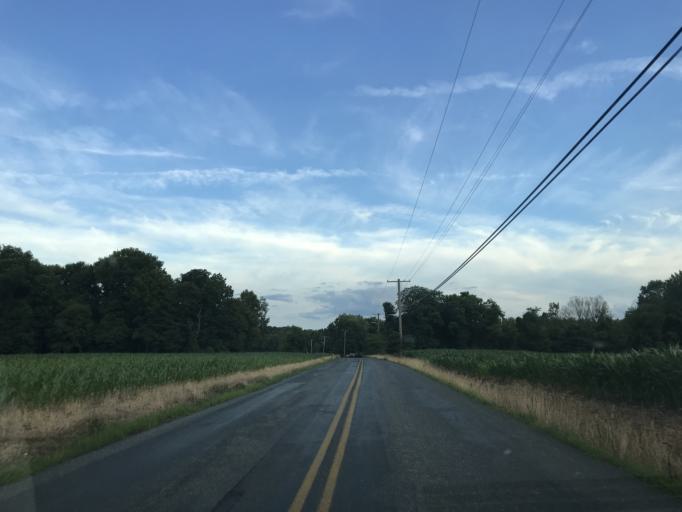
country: US
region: Maryland
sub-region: Harford County
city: Riverside
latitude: 39.5350
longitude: -76.2240
